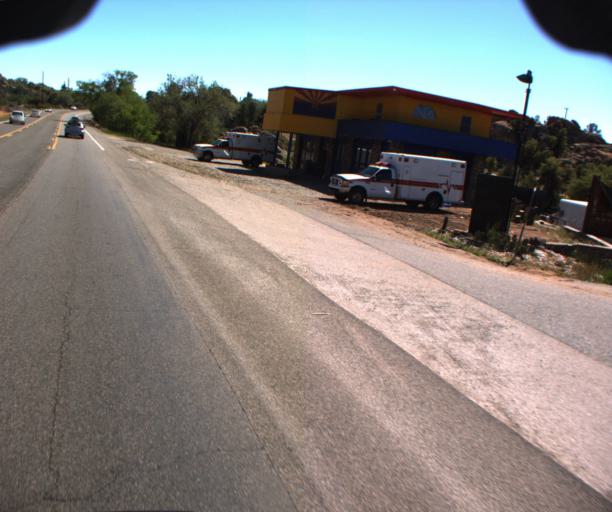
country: US
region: Arizona
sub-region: Yavapai County
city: Prescott
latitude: 34.6016
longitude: -112.4244
